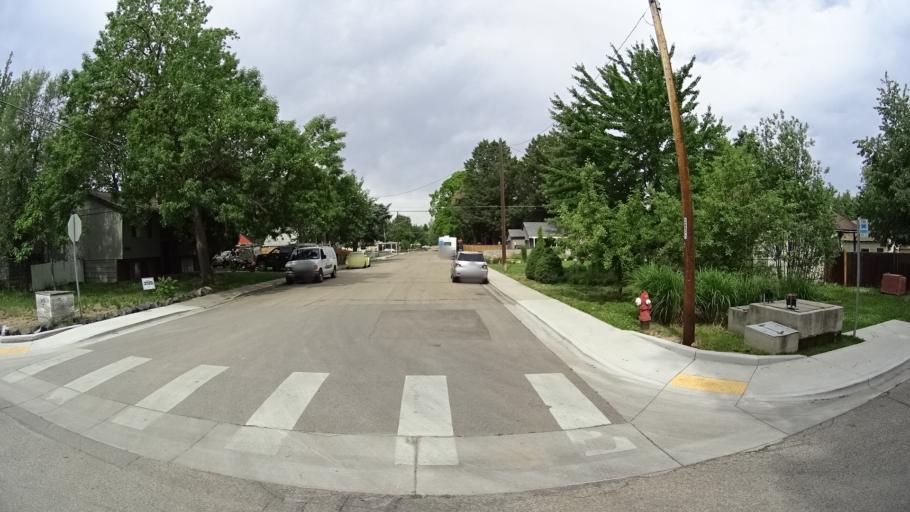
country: US
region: Idaho
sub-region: Ada County
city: Boise
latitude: 43.5839
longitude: -116.2237
